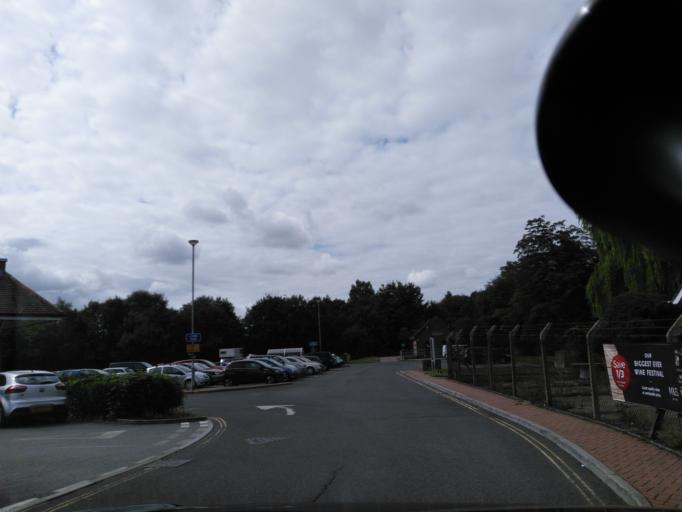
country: GB
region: England
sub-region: Dorset
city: Blandford Forum
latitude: 50.8562
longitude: -2.1597
